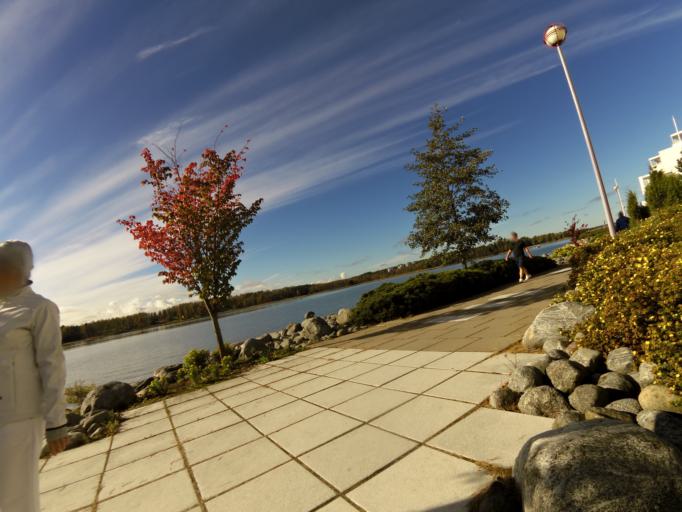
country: FI
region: Uusimaa
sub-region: Helsinki
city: Espoo
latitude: 60.1515
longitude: 24.6293
